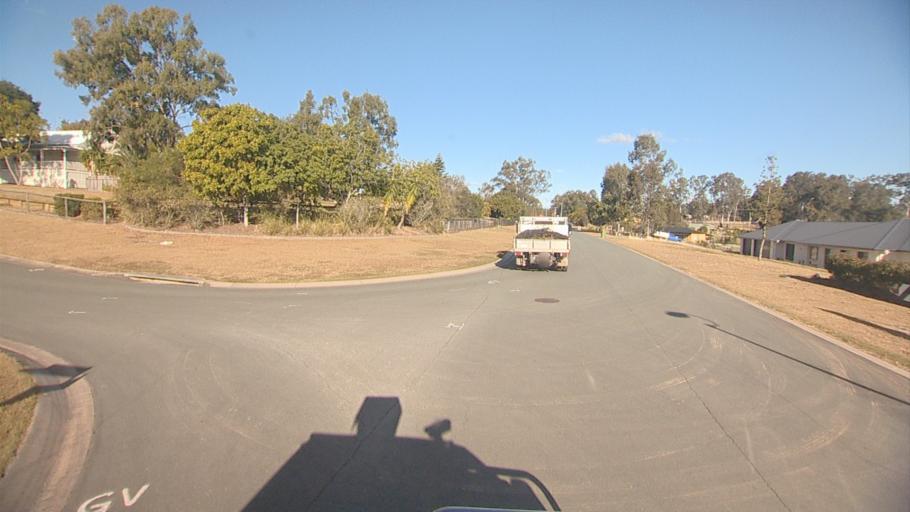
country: AU
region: Queensland
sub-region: Logan
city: North Maclean
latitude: -27.8298
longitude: 153.0041
